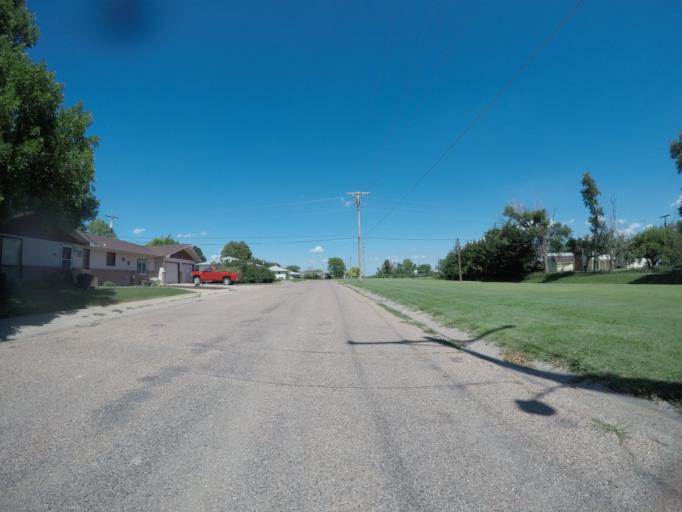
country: US
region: Kansas
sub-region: Sheridan County
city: Hoxie
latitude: 39.3588
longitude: -100.4359
